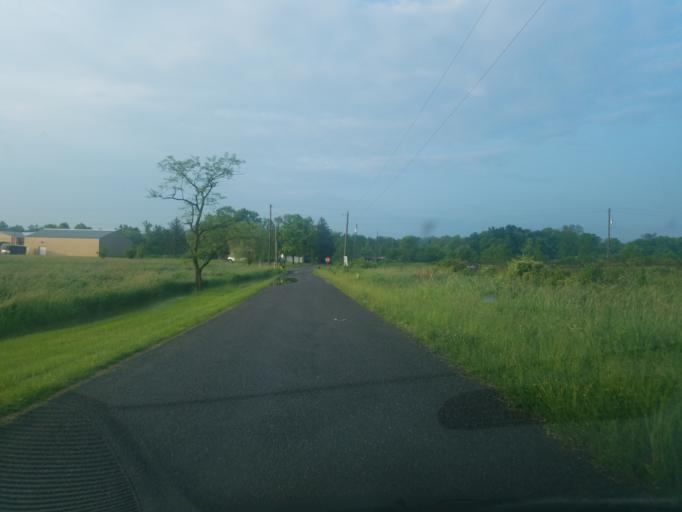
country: US
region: Ohio
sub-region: Stark County
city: Minerva
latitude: 40.7374
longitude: -80.9802
